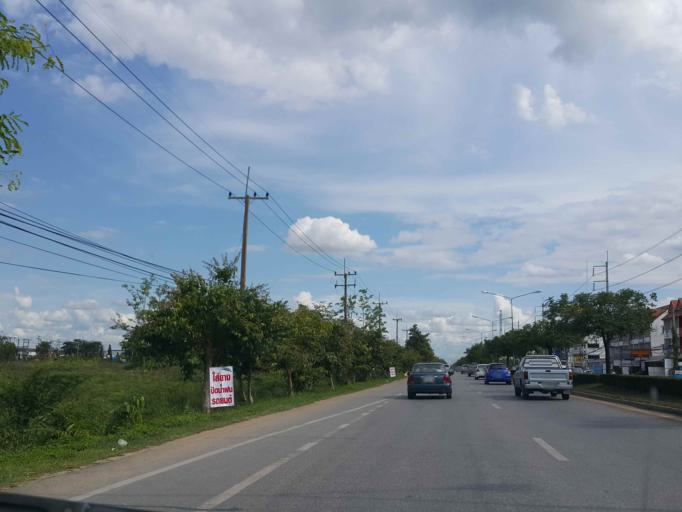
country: TH
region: Chiang Mai
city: San Sai
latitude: 18.8635
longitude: 99.0150
